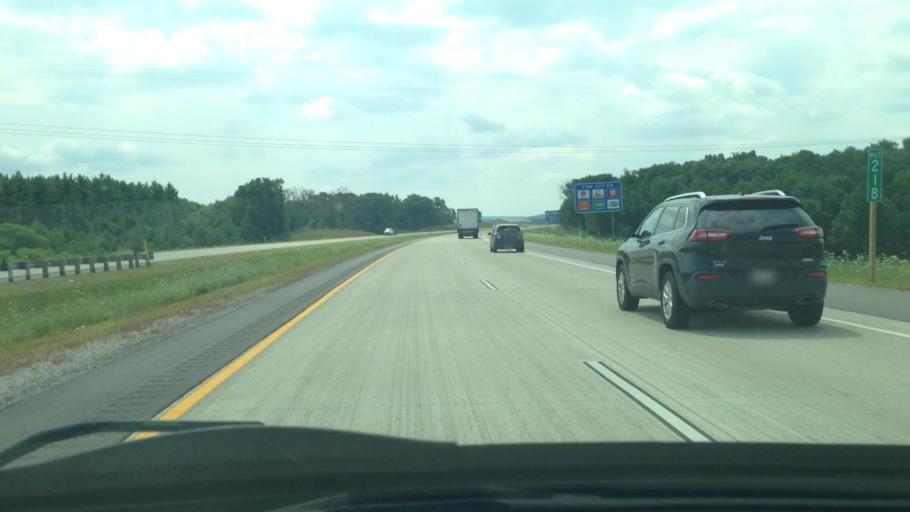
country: US
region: Wisconsin
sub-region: Sauk County
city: West Baraboo
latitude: 43.4849
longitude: -89.7763
